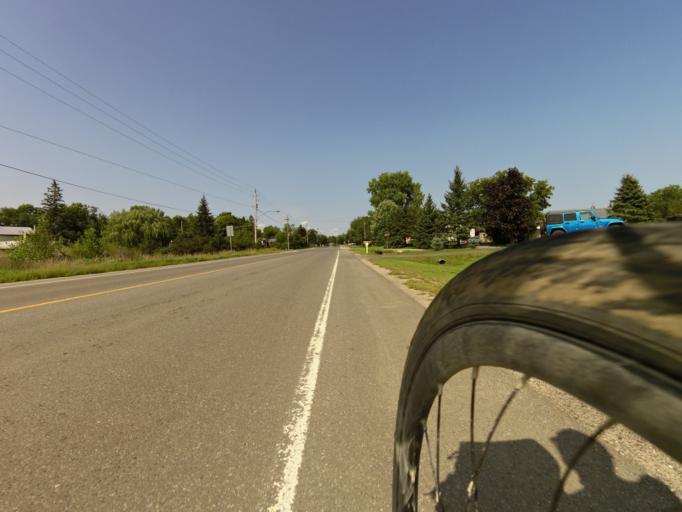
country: CA
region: Ontario
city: Skatepark
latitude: 44.2716
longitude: -76.7163
